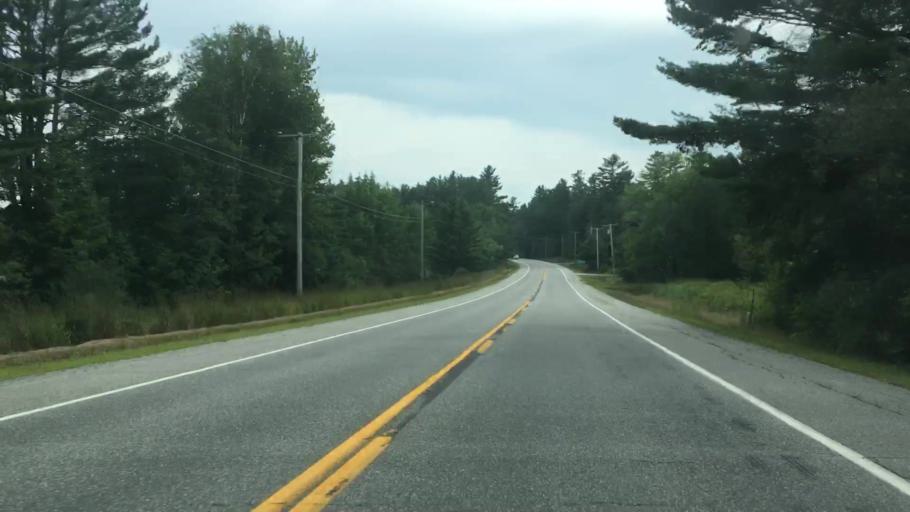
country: US
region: Maine
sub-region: Oxford County
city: Bethel
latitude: 44.4665
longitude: -70.8008
